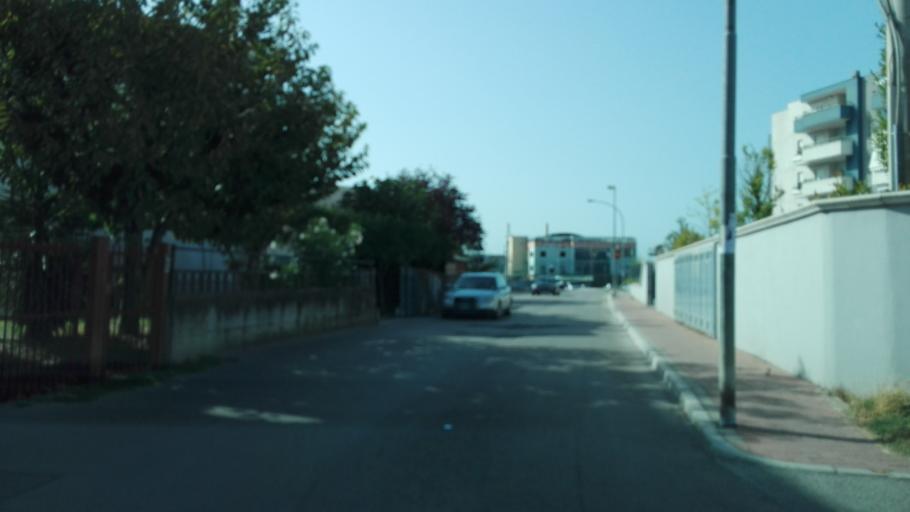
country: IT
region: Abruzzo
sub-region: Provincia di Pescara
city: Montesilvano Marina
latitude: 42.5102
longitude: 14.1383
